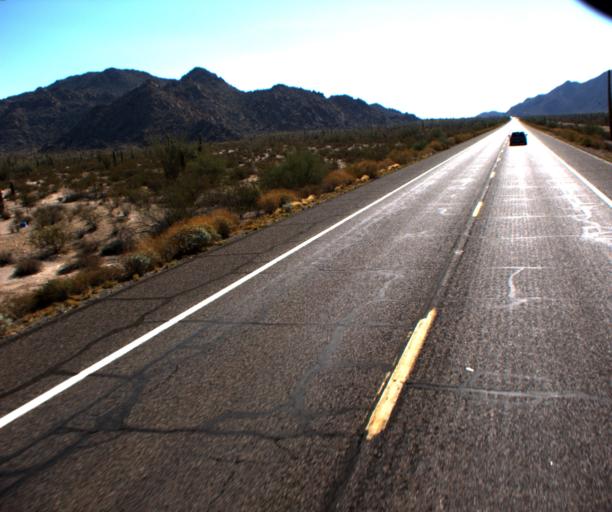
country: US
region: Arizona
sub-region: Pinal County
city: Sacaton
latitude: 33.0046
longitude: -111.7220
